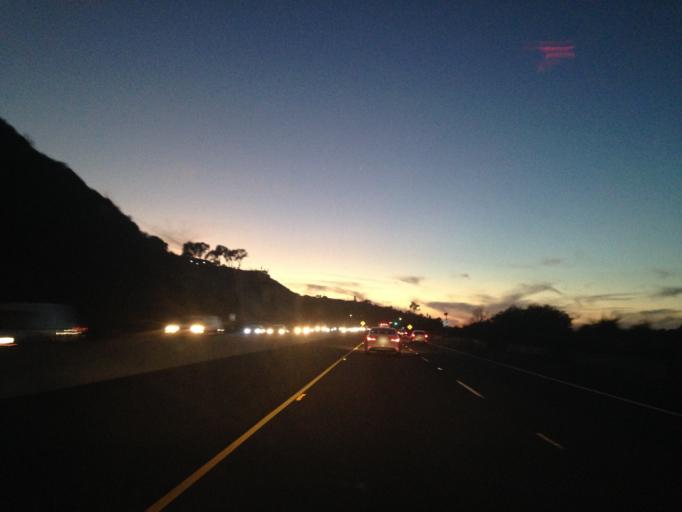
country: US
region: California
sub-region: San Diego County
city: Camp Pendleton South
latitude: 33.2136
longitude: -117.3621
